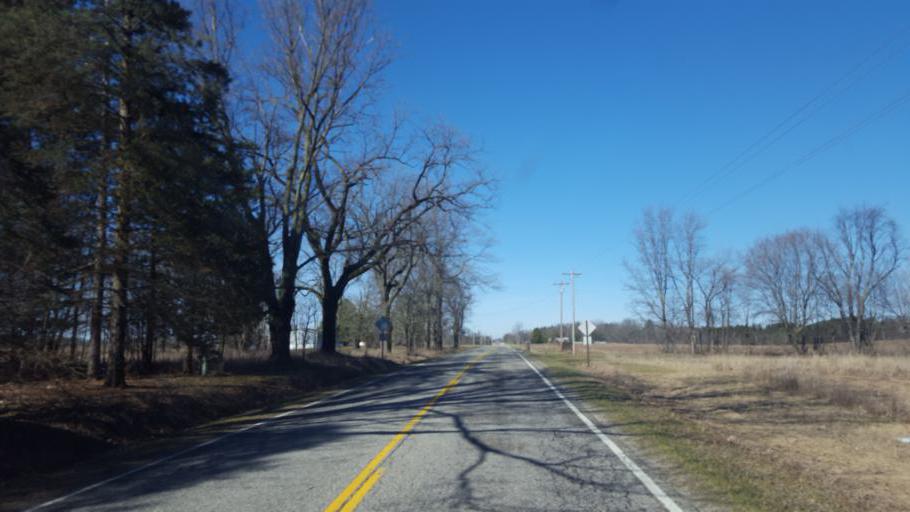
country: US
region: Michigan
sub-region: Montcalm County
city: Edmore
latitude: 43.4878
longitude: -85.0289
